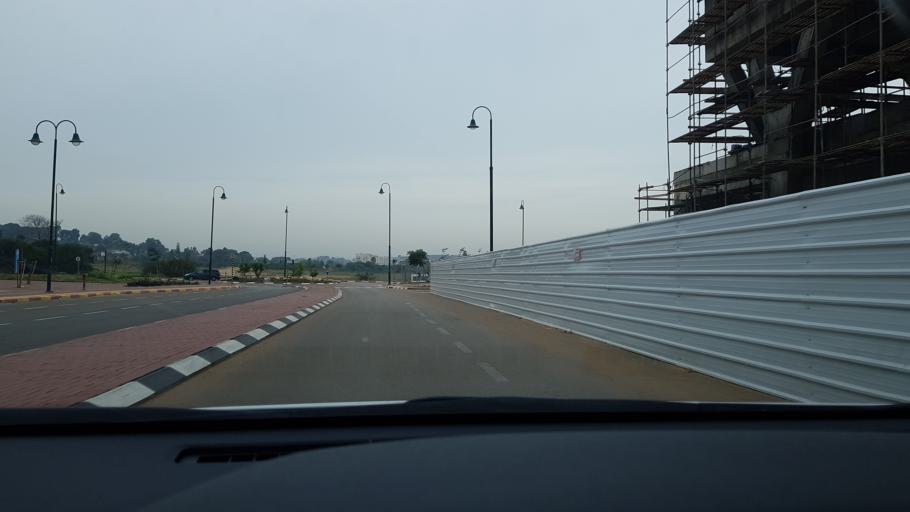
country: IL
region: Central District
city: Ness Ziona
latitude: 31.9183
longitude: 34.8049
